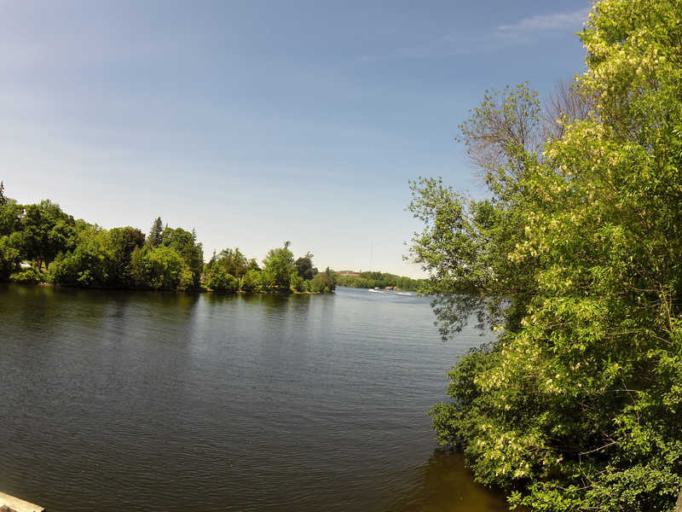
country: CA
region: Ontario
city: Peterborough
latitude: 44.2915
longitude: -78.3066
